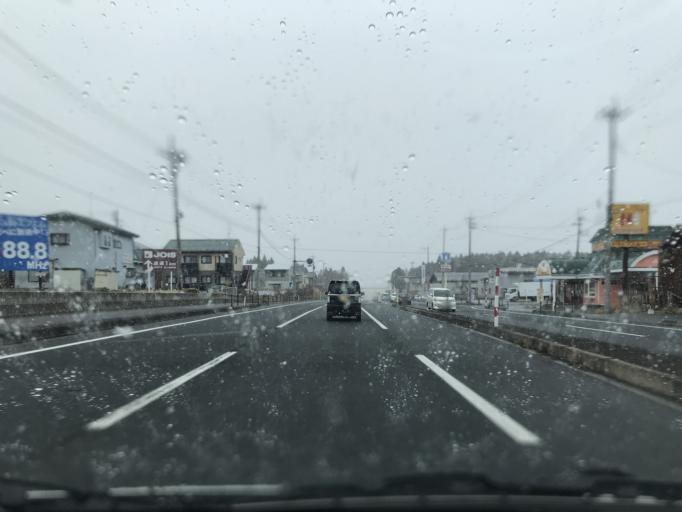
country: JP
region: Iwate
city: Kitakami
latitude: 39.2630
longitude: 141.0990
